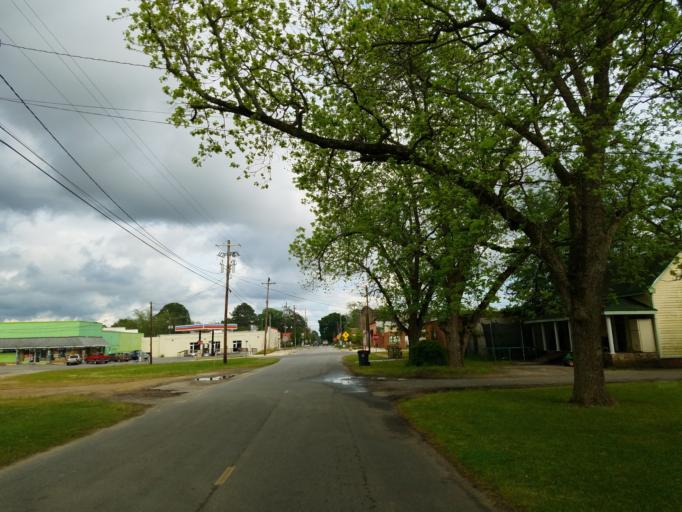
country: US
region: Georgia
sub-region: Dooly County
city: Unadilla
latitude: 32.2632
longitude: -83.7370
